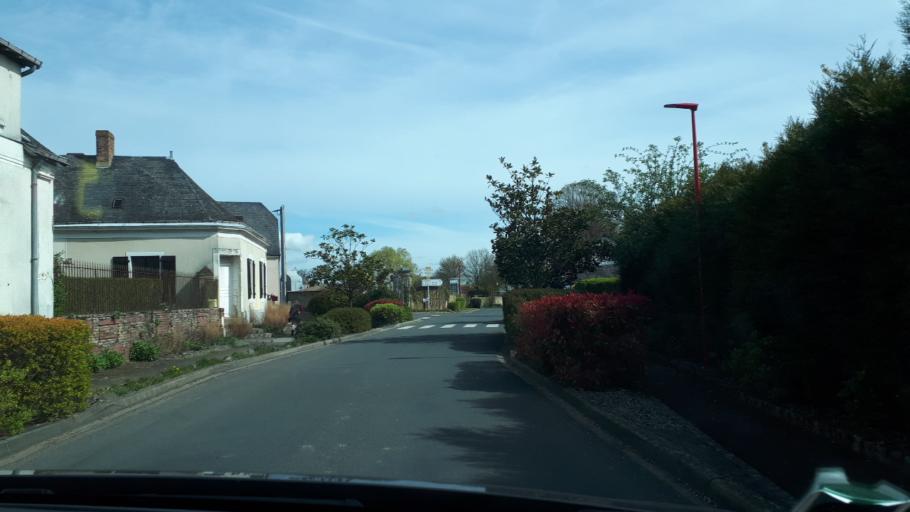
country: FR
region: Pays de la Loire
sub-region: Departement de la Sarthe
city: Yvre-le-Polin
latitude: 47.8213
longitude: 0.1550
